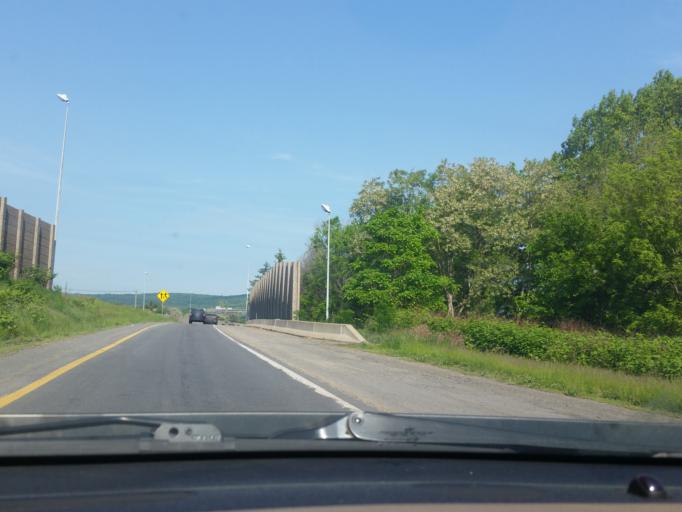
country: US
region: Pennsylvania
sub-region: Luzerne County
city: Forty Fort
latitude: 41.2761
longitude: -75.8826
